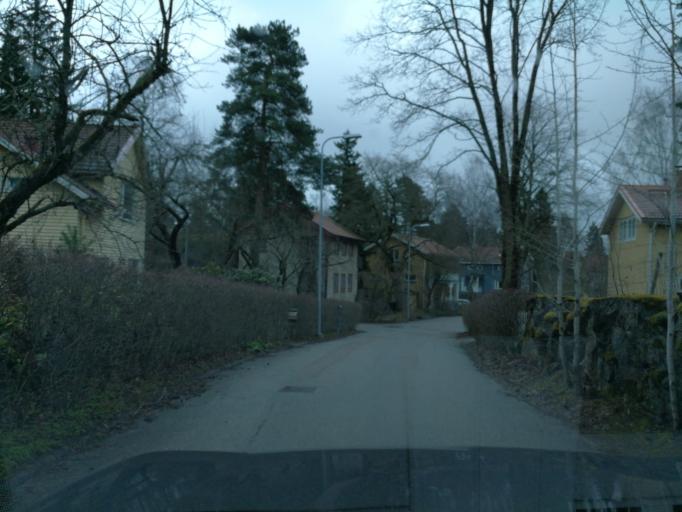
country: FI
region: Uusimaa
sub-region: Helsinki
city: Helsinki
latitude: 60.2204
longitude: 24.9562
